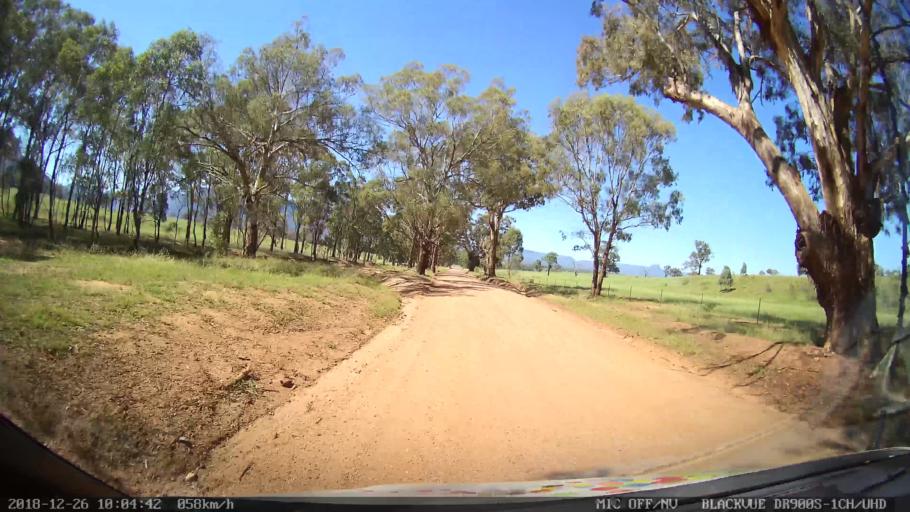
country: AU
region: New South Wales
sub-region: Mid-Western Regional
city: Kandos
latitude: -33.0724
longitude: 150.2132
